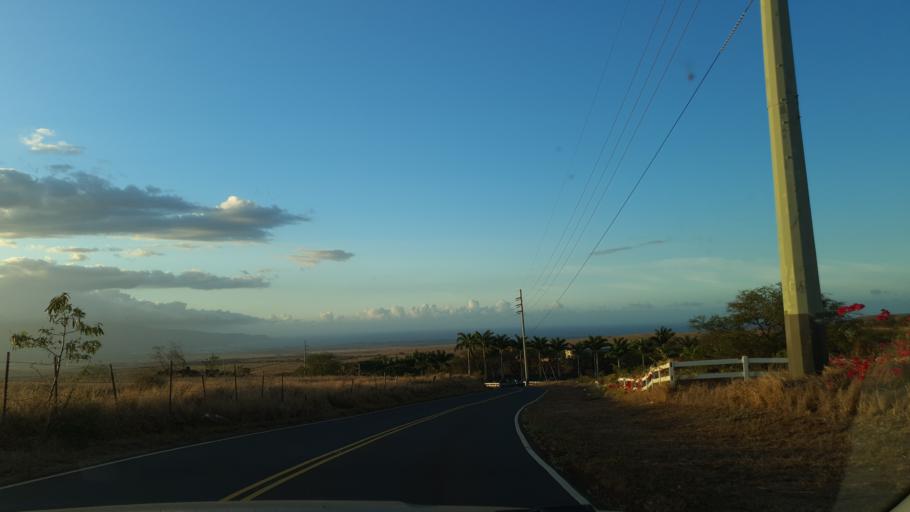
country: US
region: Hawaii
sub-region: Maui County
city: Pukalani
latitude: 20.7982
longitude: -156.3718
